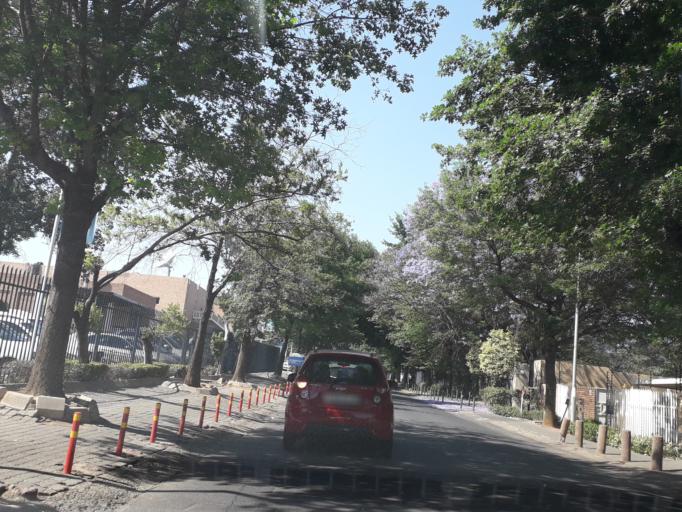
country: ZA
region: Gauteng
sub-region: City of Johannesburg Metropolitan Municipality
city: Johannesburg
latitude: -26.1006
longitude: 28.0008
